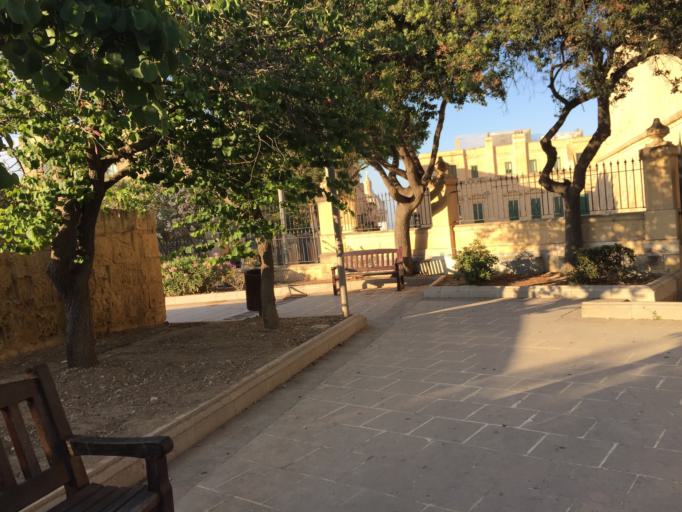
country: MT
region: Il-Furjana
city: Floriana
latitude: 35.8975
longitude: 14.5082
